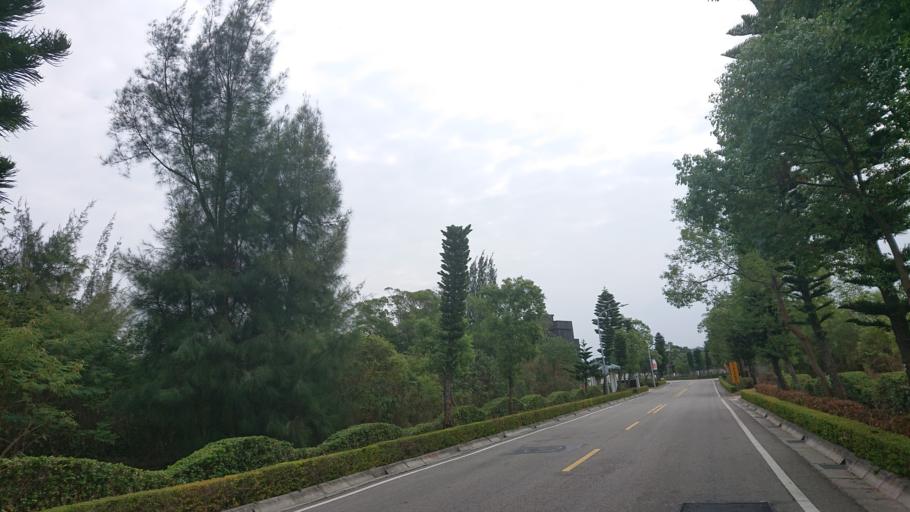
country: TW
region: Fukien
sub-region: Kinmen
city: Jincheng
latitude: 24.4129
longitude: 118.2889
